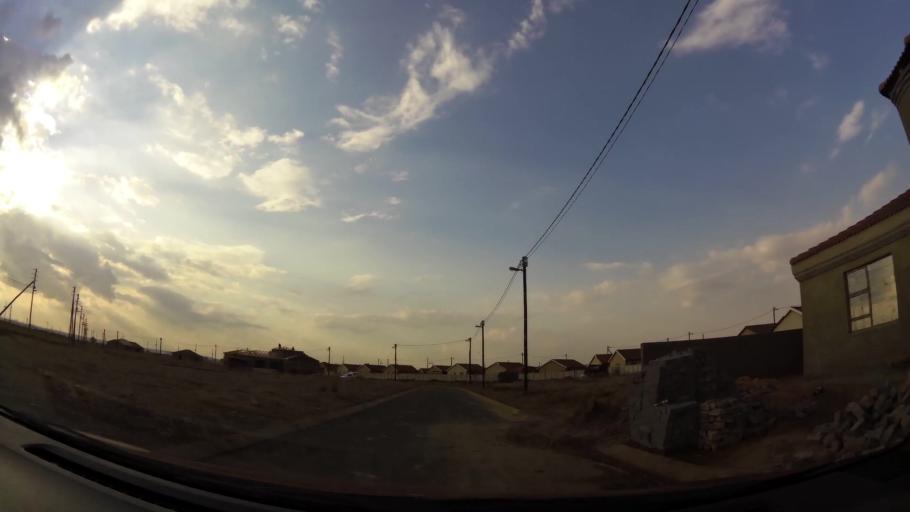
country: ZA
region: Gauteng
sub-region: Sedibeng District Municipality
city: Vanderbijlpark
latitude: -26.6115
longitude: 27.8117
